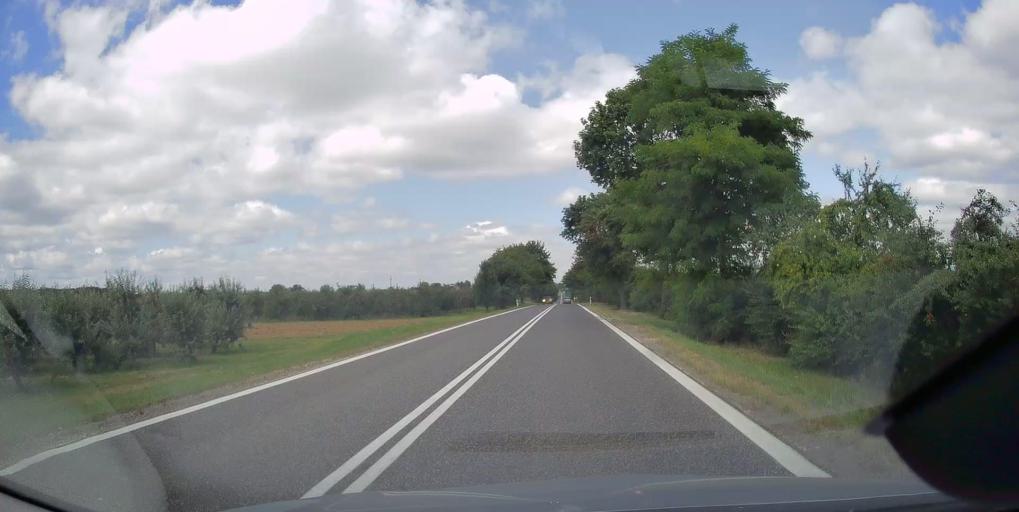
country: PL
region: Swietokrzyskie
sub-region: Powiat sandomierski
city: Loniow
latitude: 50.5668
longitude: 21.5136
